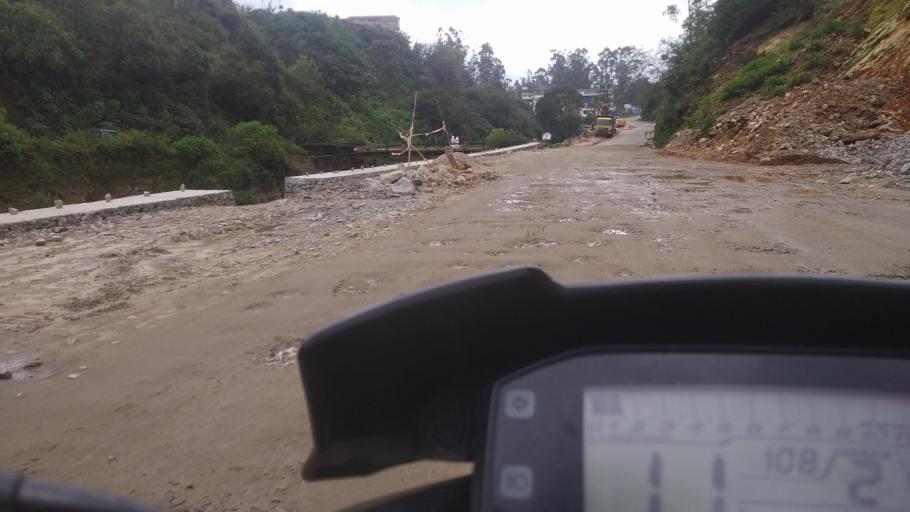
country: IN
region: Kerala
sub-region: Idukki
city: Munnar
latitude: 10.0846
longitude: 77.0621
